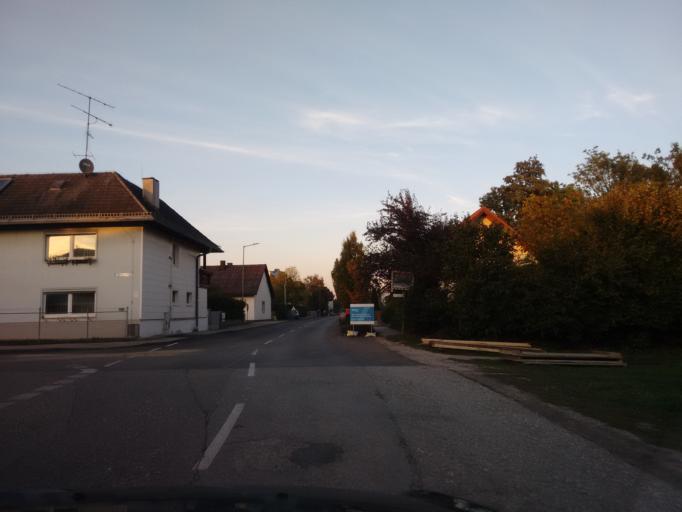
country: AT
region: Upper Austria
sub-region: Wels Stadt
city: Wels
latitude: 48.1643
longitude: 13.9861
